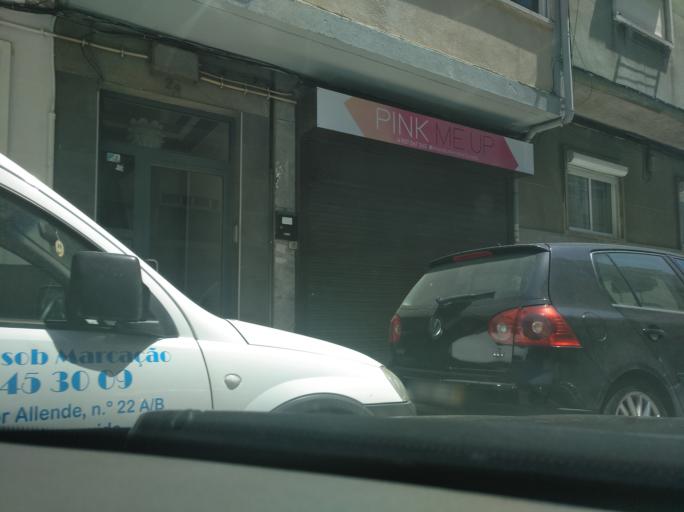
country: PT
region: Lisbon
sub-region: Loures
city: Moscavide
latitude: 38.7765
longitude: -9.1002
